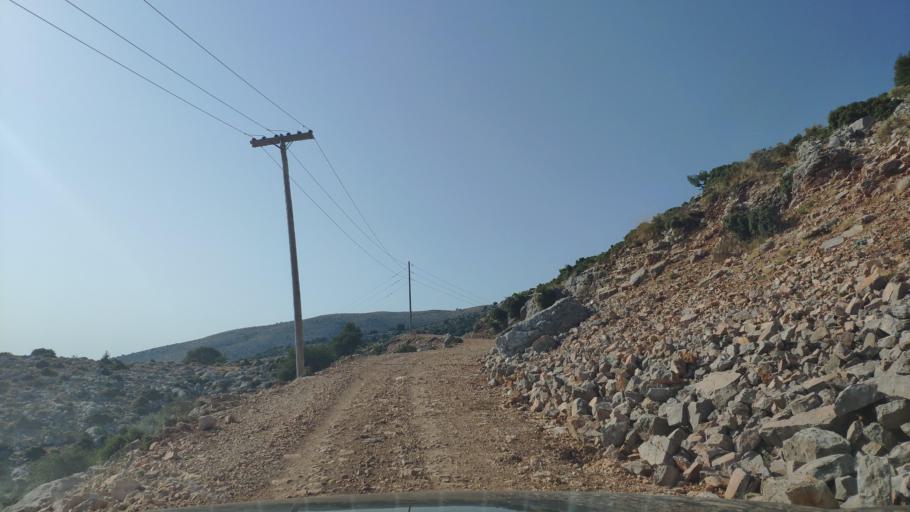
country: GR
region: West Greece
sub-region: Nomos Aitolias kai Akarnanias
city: Monastirakion
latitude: 38.8268
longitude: 20.9793
